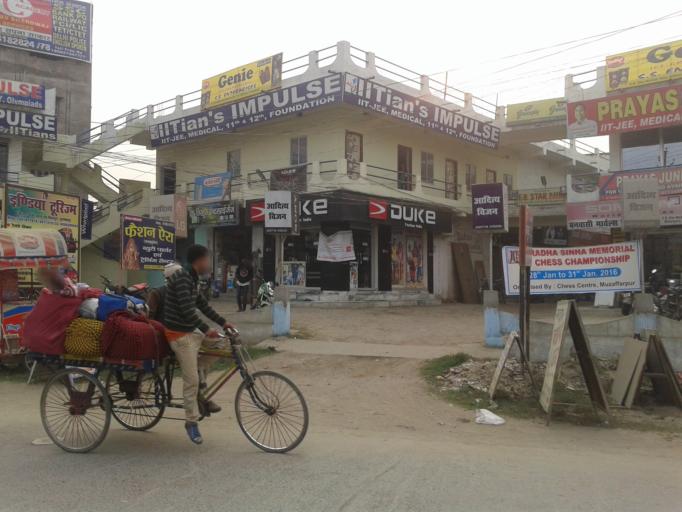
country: IN
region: Bihar
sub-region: Muzaffarpur
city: Muzaffarpur
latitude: 26.1057
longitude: 85.3983
